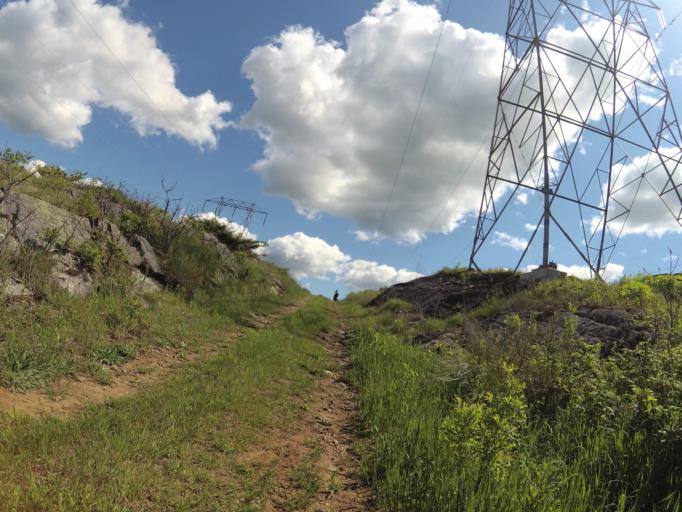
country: CA
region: Ontario
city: Renfrew
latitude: 45.0446
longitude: -76.7688
